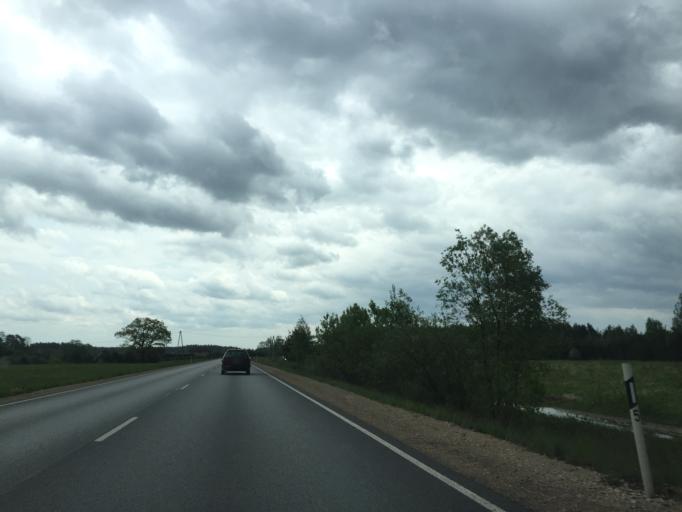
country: LV
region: Salaspils
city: Salaspils
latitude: 56.8989
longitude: 24.4231
